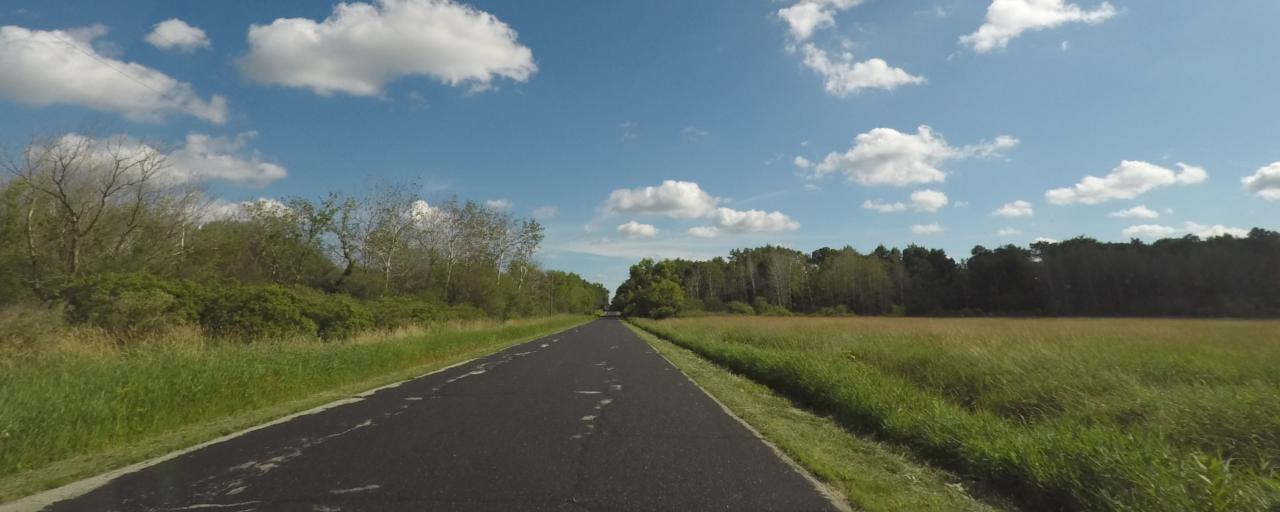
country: US
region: Wisconsin
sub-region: Rock County
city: Edgerton
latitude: 42.8755
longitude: -89.1321
